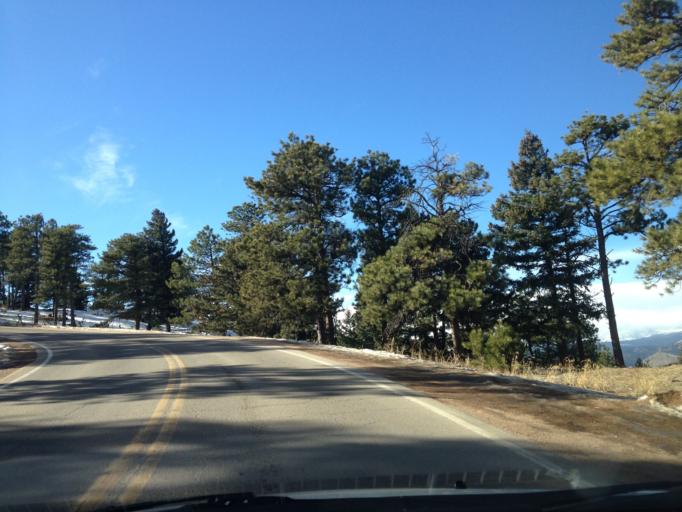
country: US
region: Colorado
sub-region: Boulder County
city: Boulder
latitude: 39.9909
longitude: -105.3193
